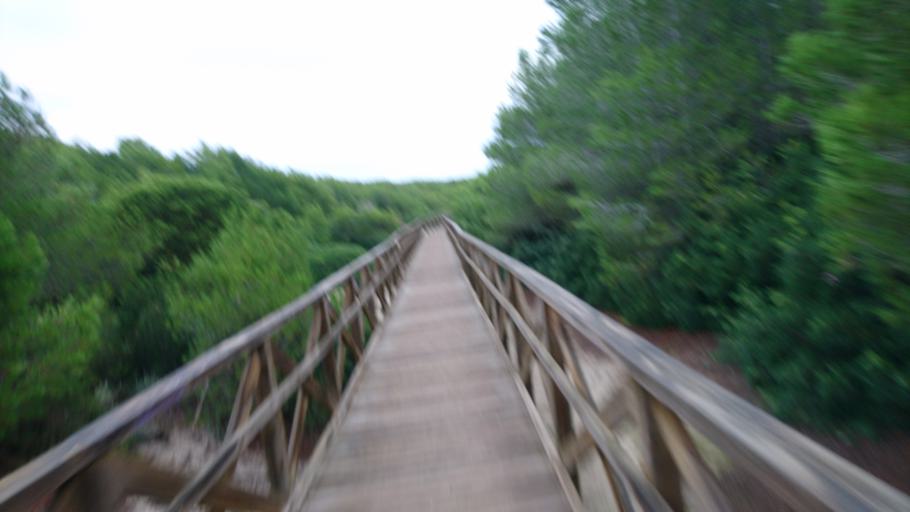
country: ES
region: Balearic Islands
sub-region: Illes Balears
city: Port d'Alcudia
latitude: 39.7749
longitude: 3.1408
